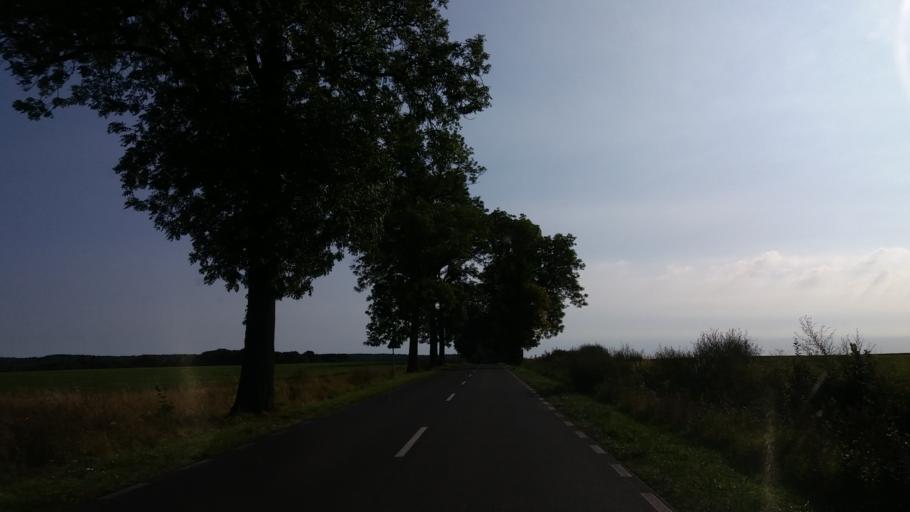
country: PL
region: West Pomeranian Voivodeship
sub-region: Powiat choszczenski
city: Choszczno
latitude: 53.1774
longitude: 15.5018
